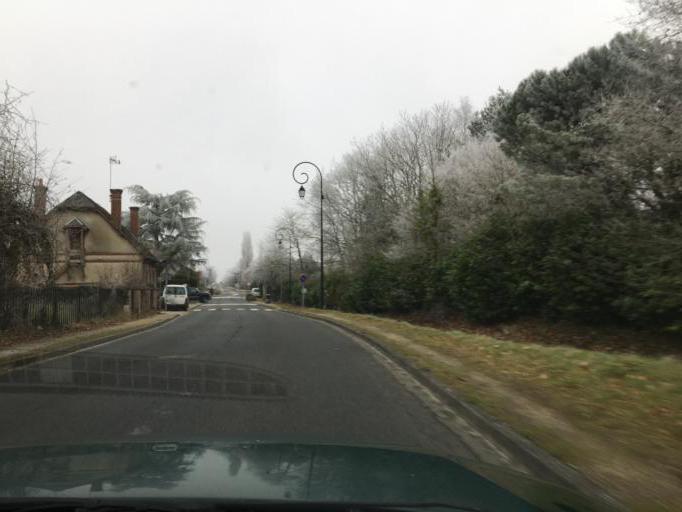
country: FR
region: Centre
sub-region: Departement du Loiret
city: Ligny-le-Ribault
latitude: 47.6855
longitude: 1.7832
